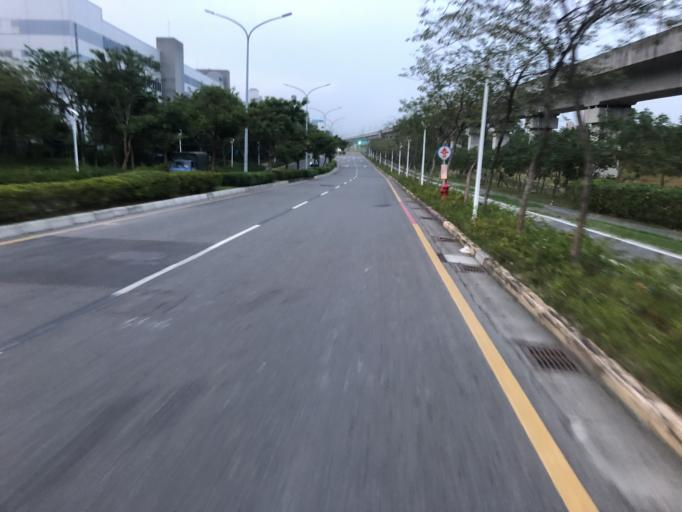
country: TW
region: Taiwan
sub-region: Tainan
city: Tainan
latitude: 23.0915
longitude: 120.2862
